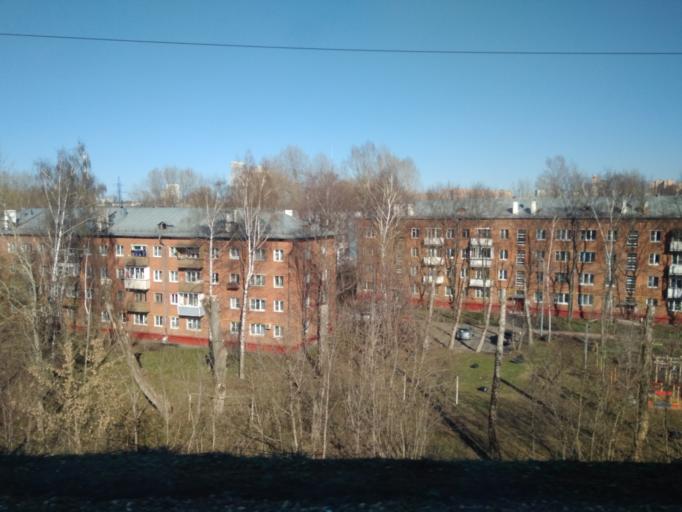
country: RU
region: Moscow
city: Pokrovskoye-Streshnevo
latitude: 55.8170
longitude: 37.4462
